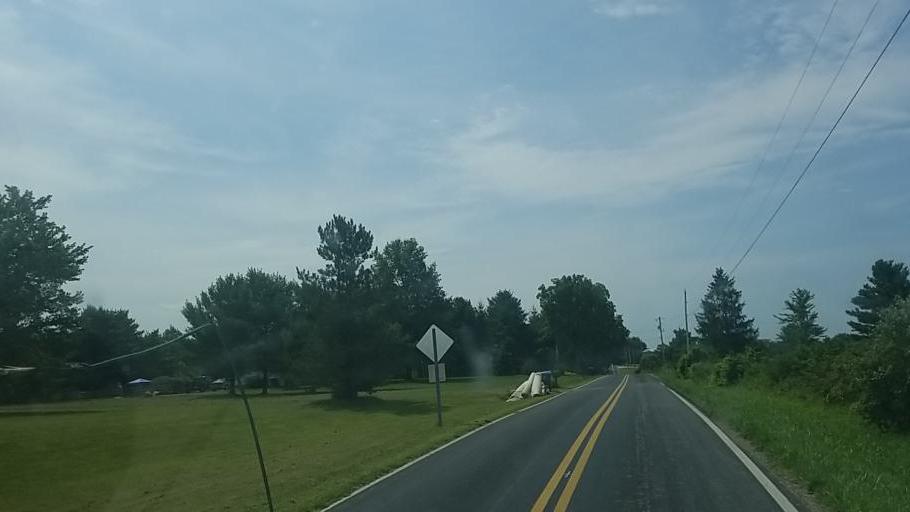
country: US
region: Ohio
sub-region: Delaware County
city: Sunbury
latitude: 40.2739
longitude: -82.8580
